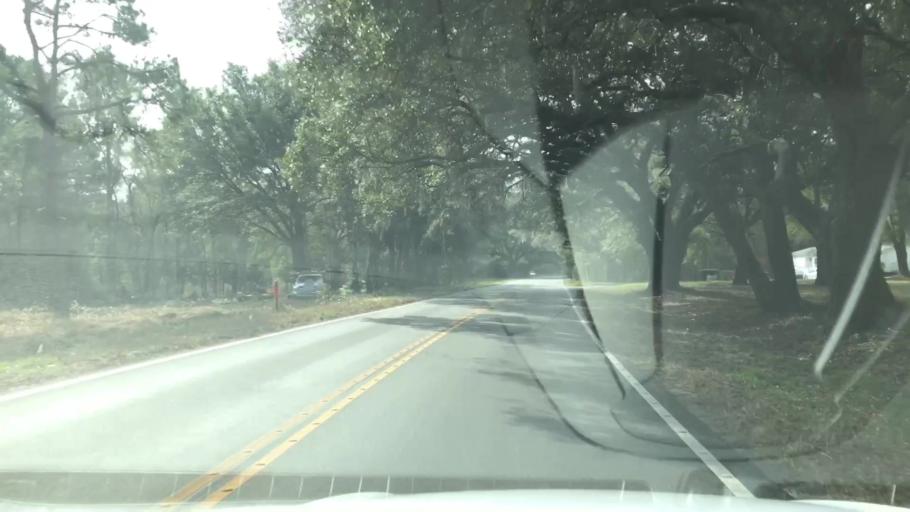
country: US
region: South Carolina
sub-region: Charleston County
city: Folly Beach
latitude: 32.6988
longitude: -80.0145
